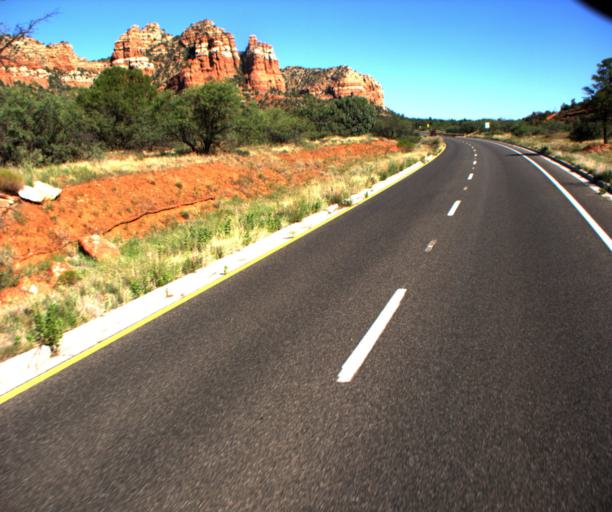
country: US
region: Arizona
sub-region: Yavapai County
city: Village of Oak Creek (Big Park)
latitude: 34.7958
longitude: -111.7650
